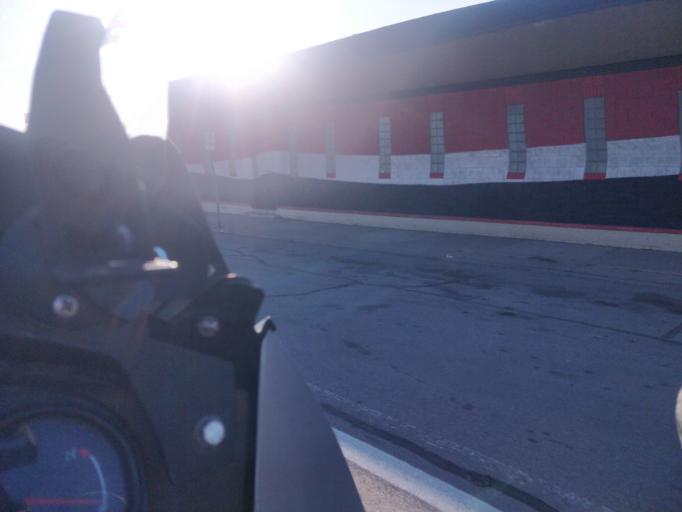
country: US
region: Michigan
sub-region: Wayne County
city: Lincoln Park
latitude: 42.2610
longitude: -83.1683
